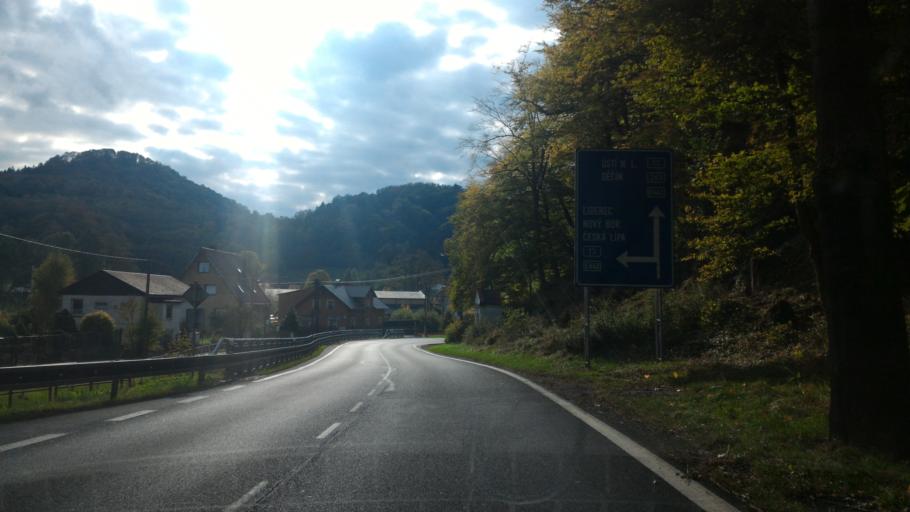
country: CZ
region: Ustecky
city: Ceska Kamenice
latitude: 50.8023
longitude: 14.4400
